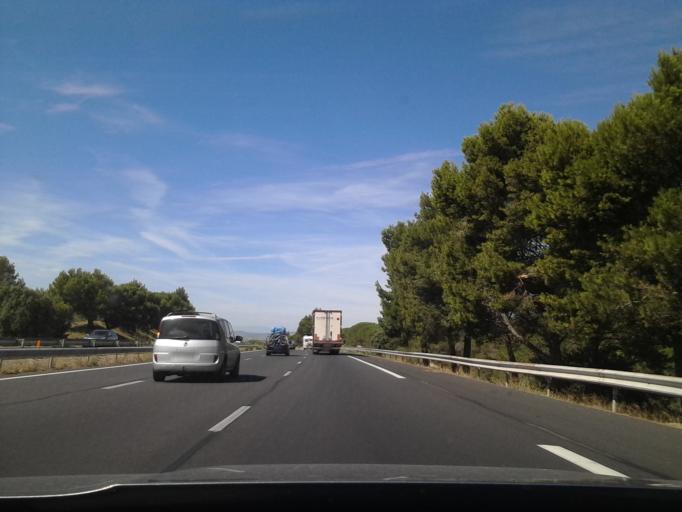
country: FR
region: Languedoc-Roussillon
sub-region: Departement de l'Aude
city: Vinassan
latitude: 43.2270
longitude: 3.1020
